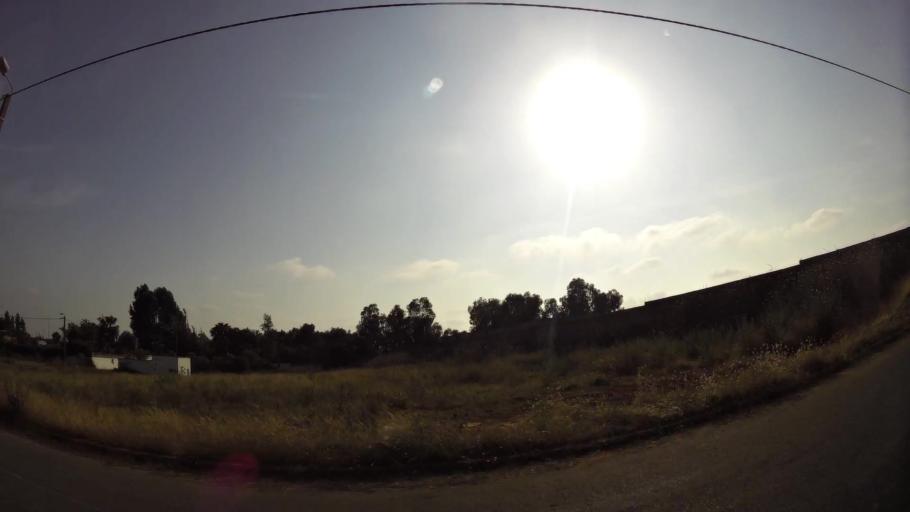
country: MA
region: Rabat-Sale-Zemmour-Zaer
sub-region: Rabat
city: Rabat
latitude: 33.9355
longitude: -6.8080
